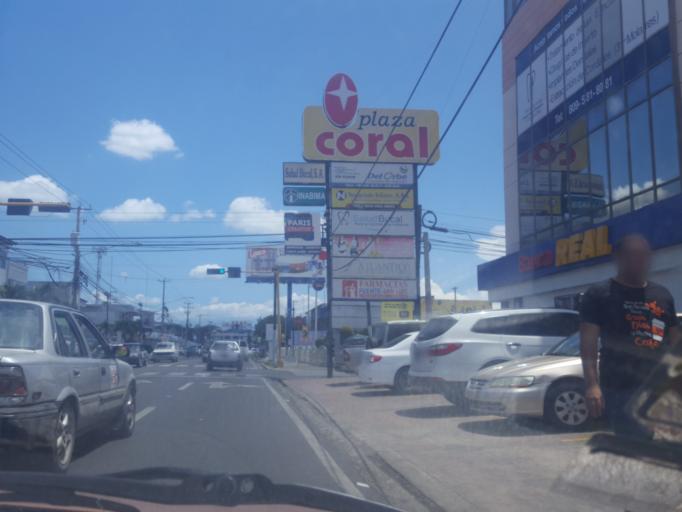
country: DO
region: Santiago
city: Santiago de los Caballeros
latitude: 19.4586
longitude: -70.7008
